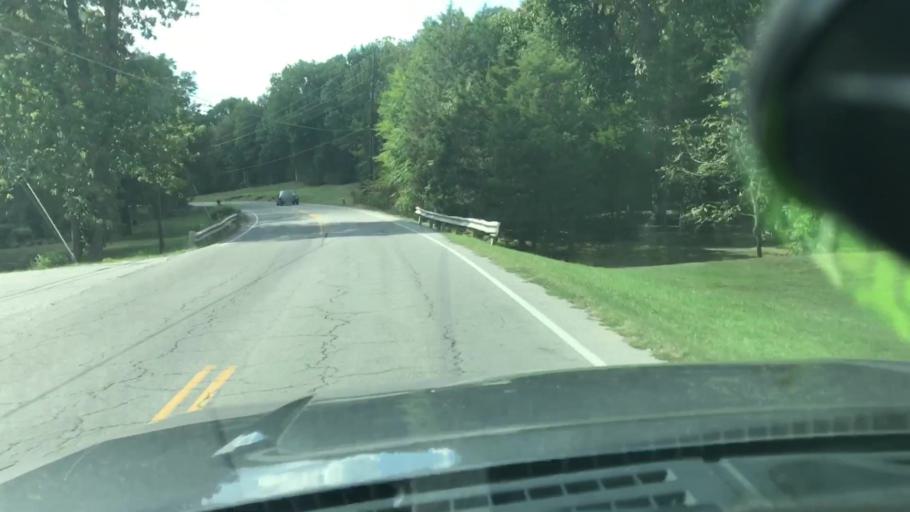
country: US
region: Tennessee
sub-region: Davidson County
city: Forest Hills
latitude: 36.0251
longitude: -86.8916
